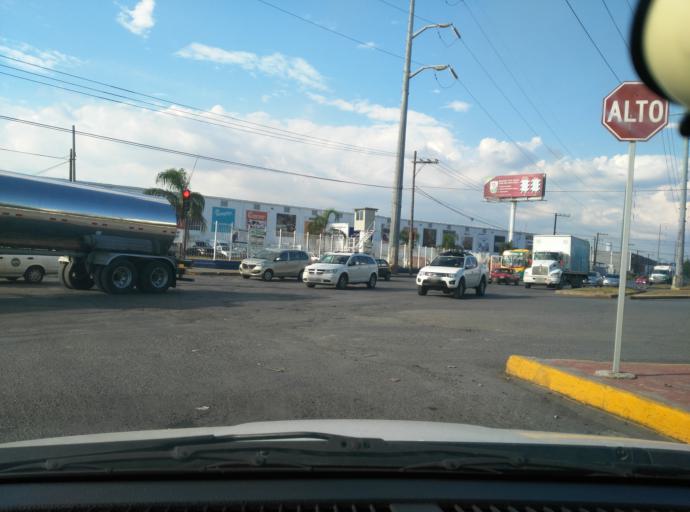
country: MX
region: Nuevo Leon
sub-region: San Nicolas de los Garza
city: San Nicolas de los Garza
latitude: 25.7304
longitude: -100.2522
